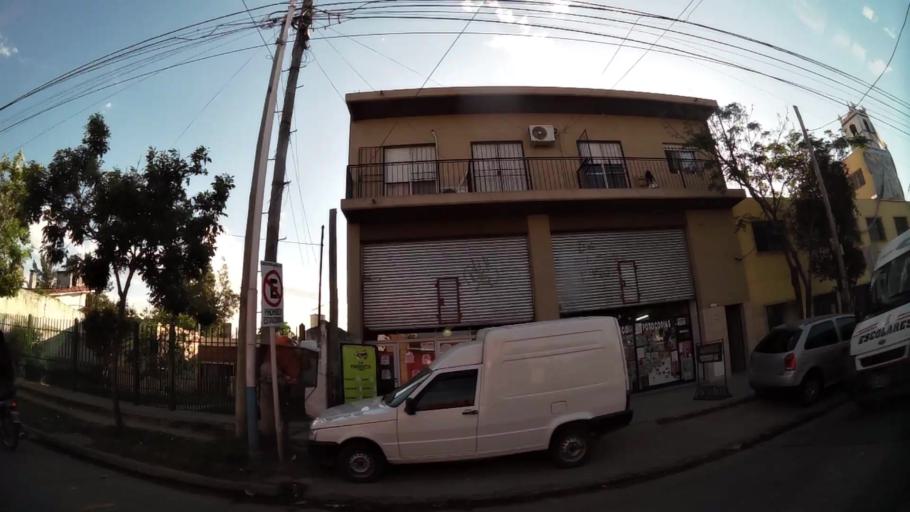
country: AR
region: Buenos Aires
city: Santa Catalina - Dique Lujan
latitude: -34.4826
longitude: -58.7295
